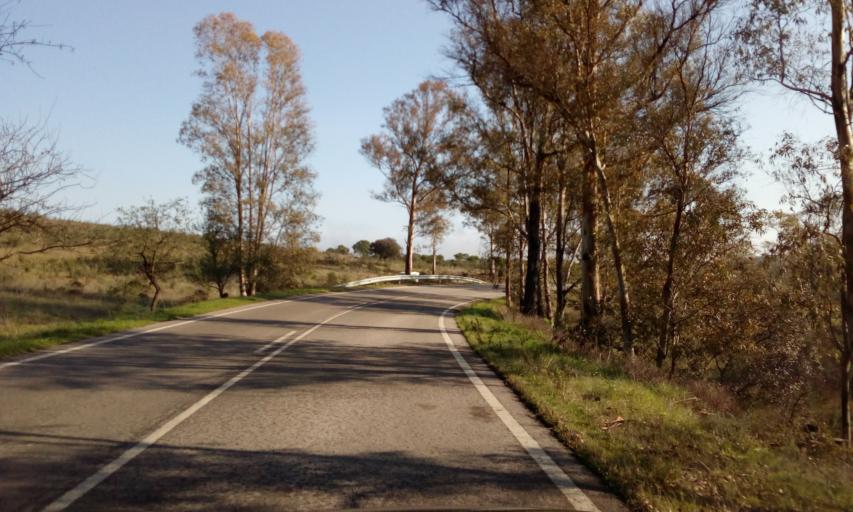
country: PT
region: Faro
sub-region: Alcoutim
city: Alcoutim
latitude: 37.4370
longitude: -7.5206
